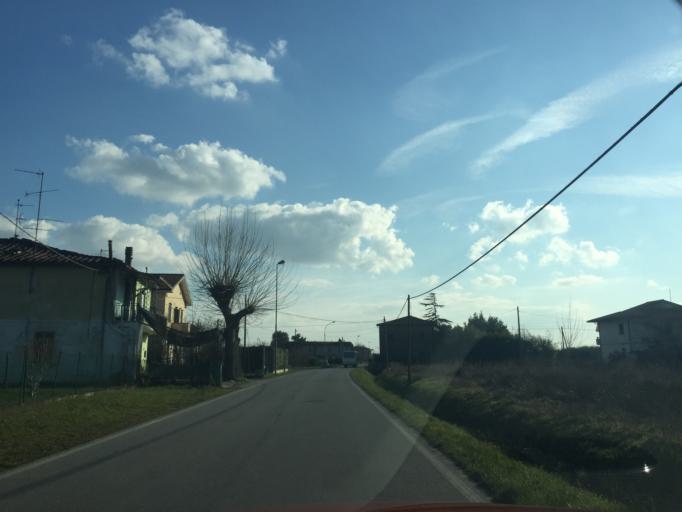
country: IT
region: Tuscany
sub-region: Provincia di Pistoia
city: Ponte Buggianese
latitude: 43.8346
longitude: 10.7430
